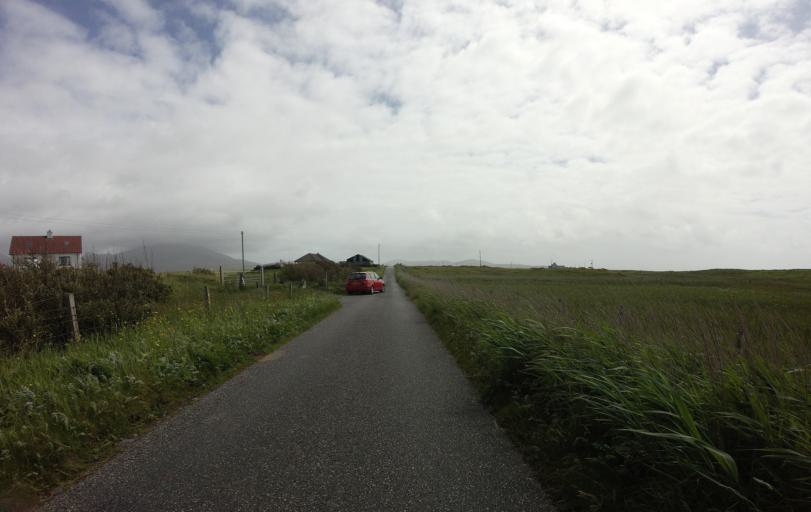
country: GB
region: Scotland
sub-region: Eilean Siar
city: Isle of South Uist
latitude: 57.2792
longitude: -7.4151
